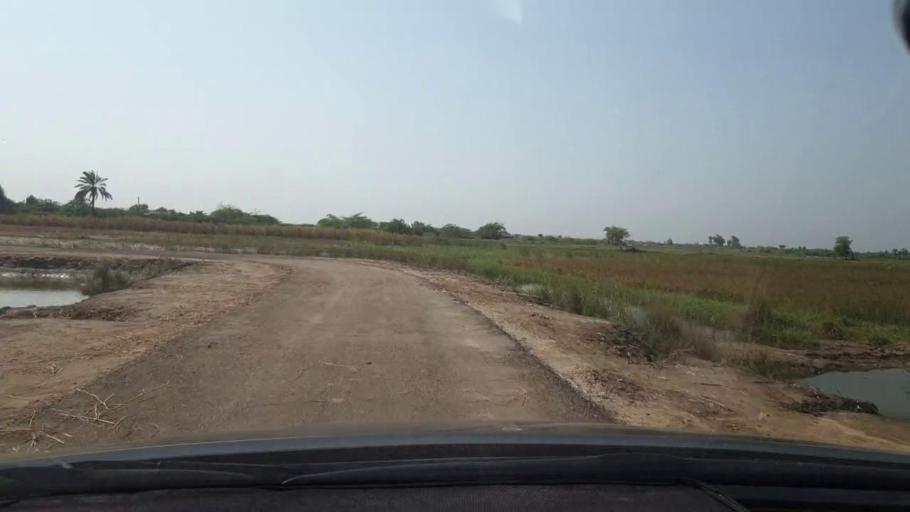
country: PK
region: Sindh
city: Tando Bago
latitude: 24.6990
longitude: 69.1062
